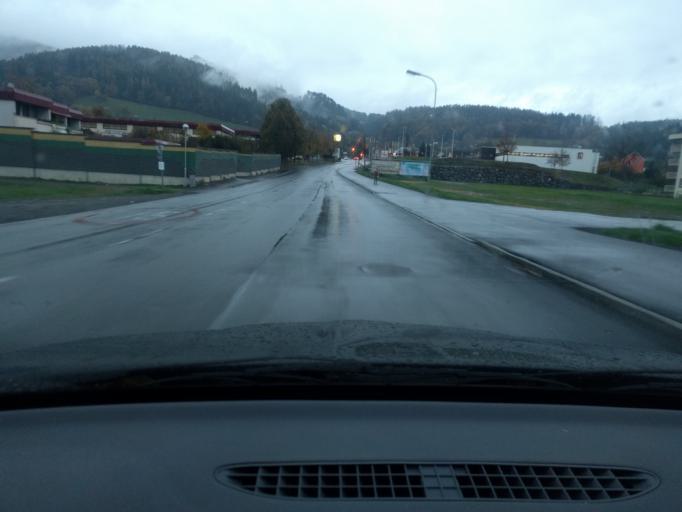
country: AT
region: Styria
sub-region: Politischer Bezirk Leoben
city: Leoben
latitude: 47.3840
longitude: 15.1058
